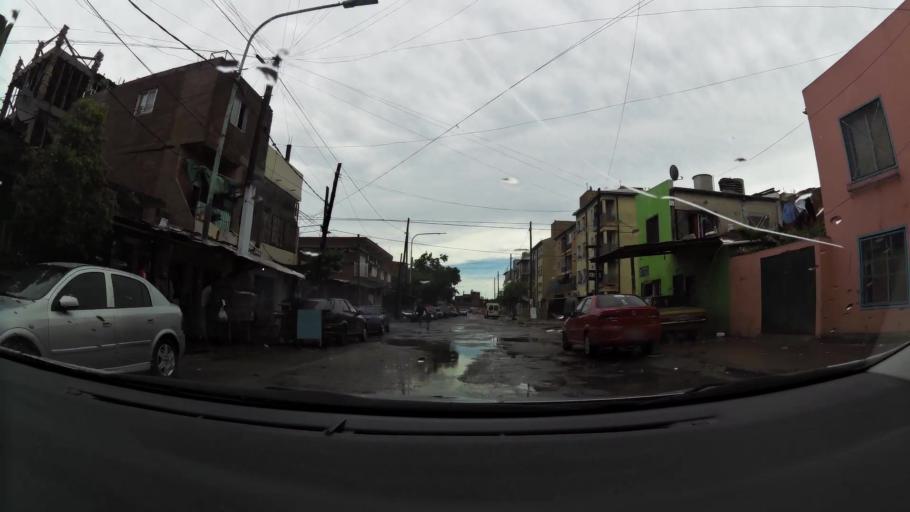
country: AR
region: Buenos Aires F.D.
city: Villa Lugano
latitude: -34.6590
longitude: -58.4545
